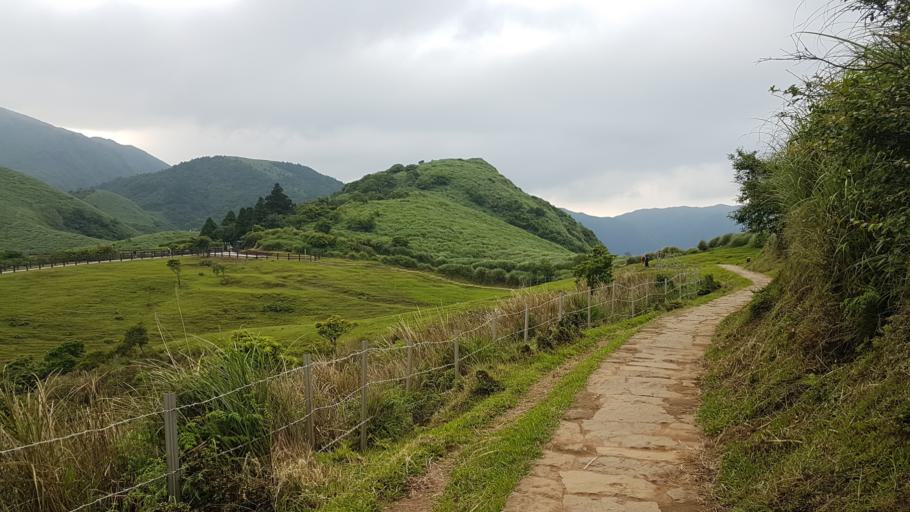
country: TW
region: Taipei
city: Taipei
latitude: 25.1663
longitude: 121.5765
